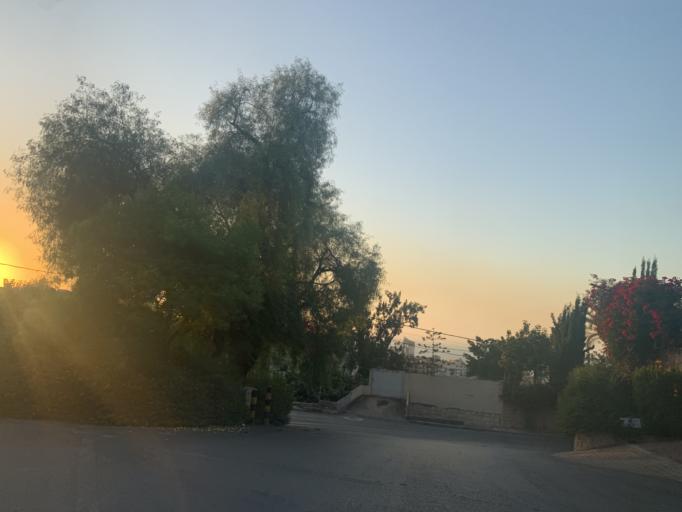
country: LB
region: Mont-Liban
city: Djounie
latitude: 33.9690
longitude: 35.6241
